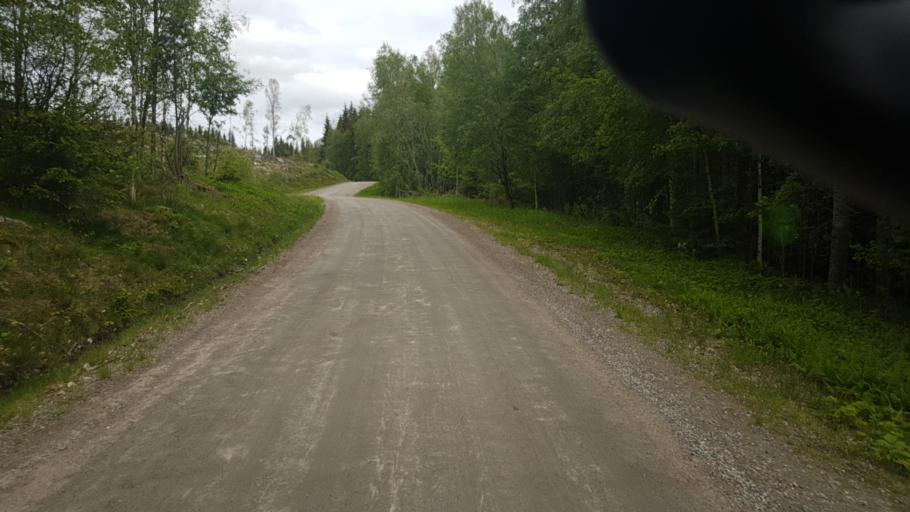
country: SE
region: Vaermland
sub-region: Eda Kommun
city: Amotfors
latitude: 59.8383
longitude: 12.5353
